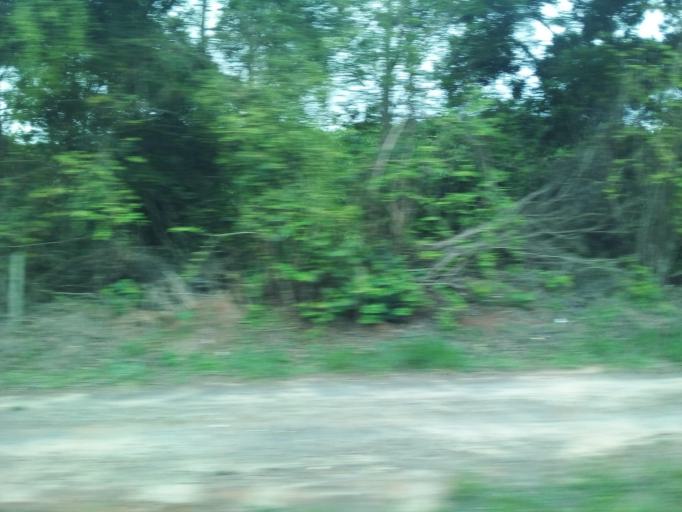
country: BR
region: Minas Gerais
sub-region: Rio Piracicaba
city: Rio Piracicaba
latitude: -19.9468
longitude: -43.1793
